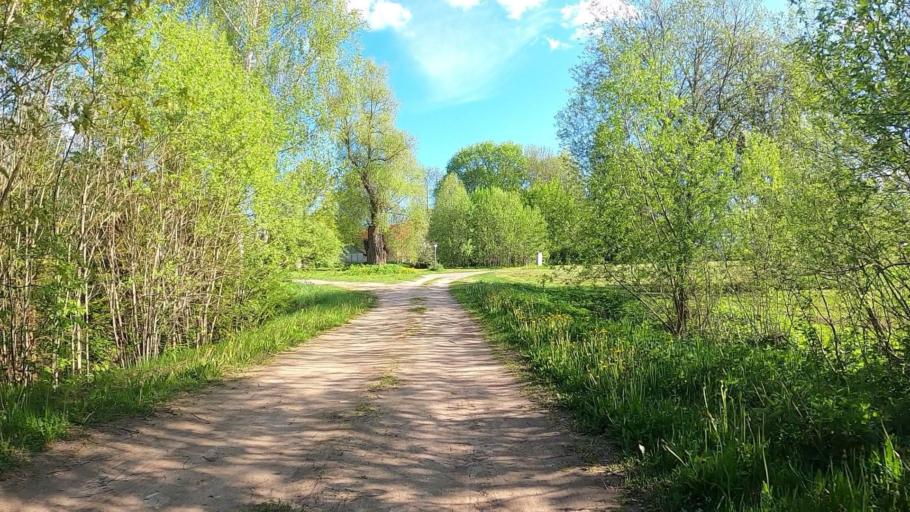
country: LV
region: Baldone
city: Baldone
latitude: 56.7667
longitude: 24.4306
